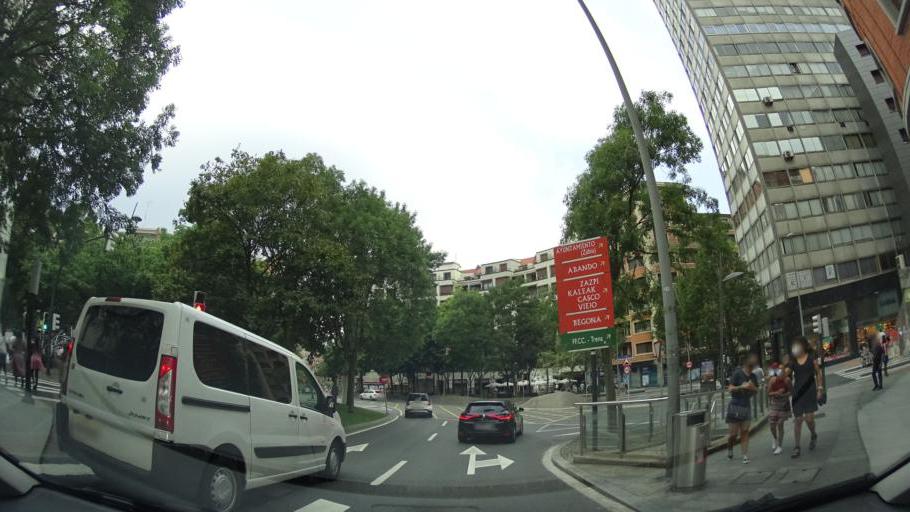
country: ES
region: Basque Country
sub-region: Bizkaia
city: Bilbao
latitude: 43.2570
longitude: -2.9337
